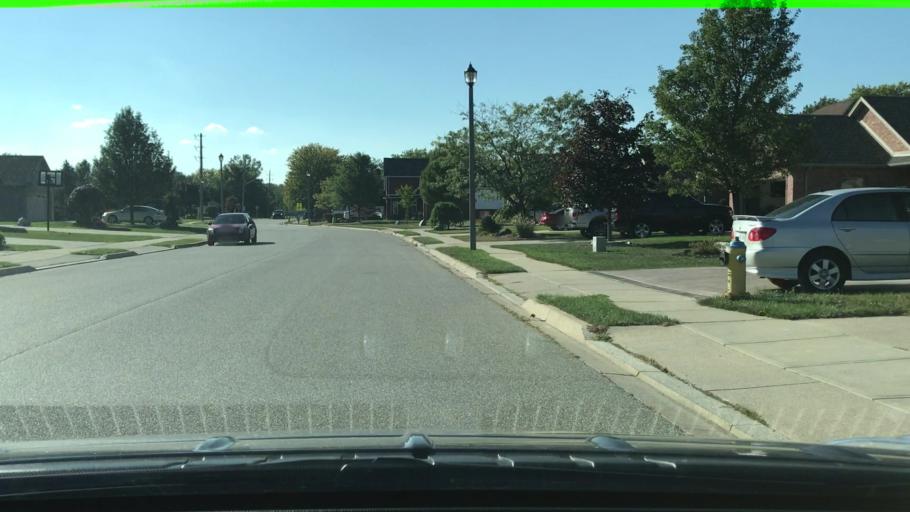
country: US
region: Michigan
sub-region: Wayne County
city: Grosse Pointe Farms
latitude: 42.2900
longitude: -82.6962
